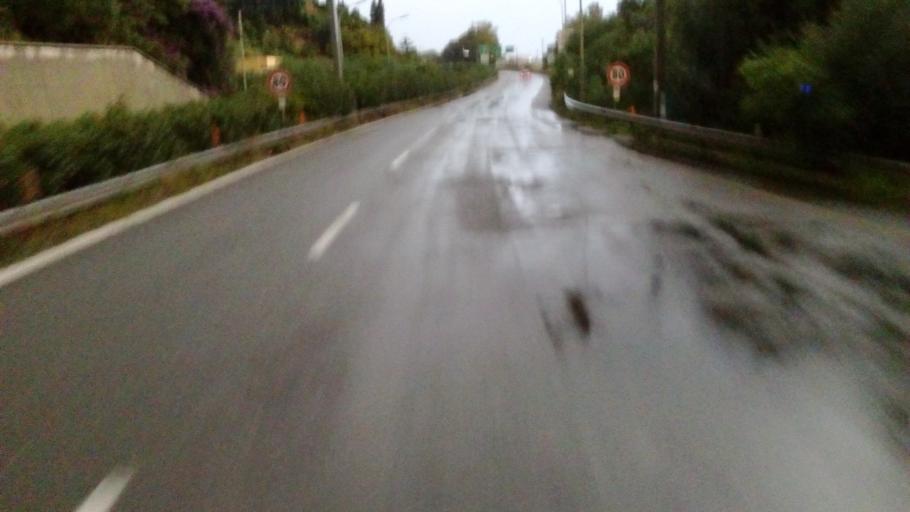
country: IT
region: Sicily
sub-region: Messina
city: Larderia
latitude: 38.1262
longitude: 15.5176
